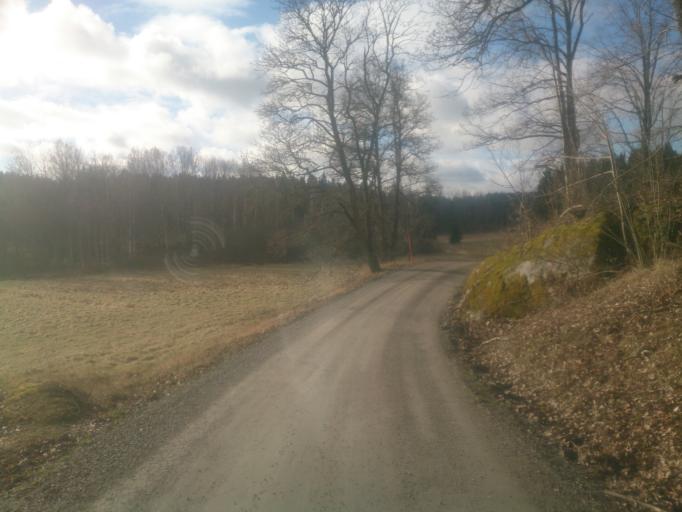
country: SE
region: OEstergoetland
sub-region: Atvidabergs Kommun
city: Atvidaberg
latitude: 58.2308
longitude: 16.1794
